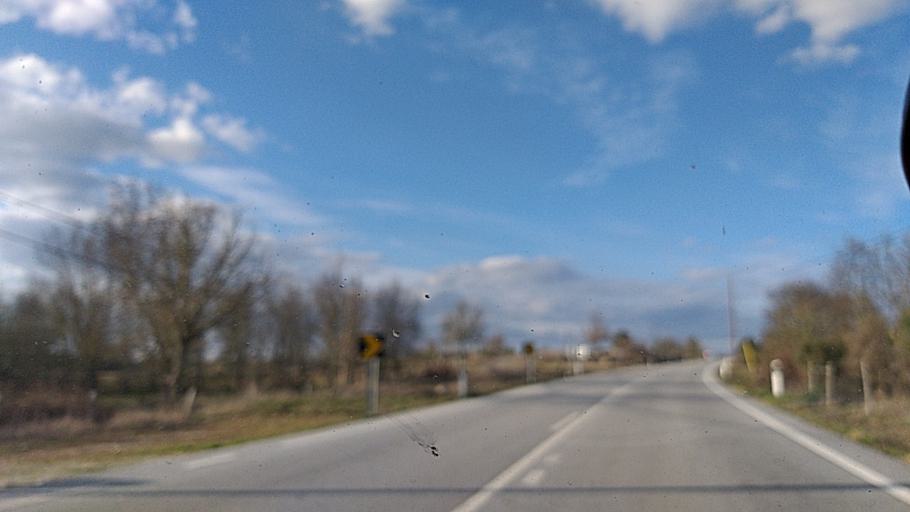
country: ES
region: Castille and Leon
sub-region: Provincia de Salamanca
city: Fuentes de Onoro
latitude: 40.6392
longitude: -6.8561
